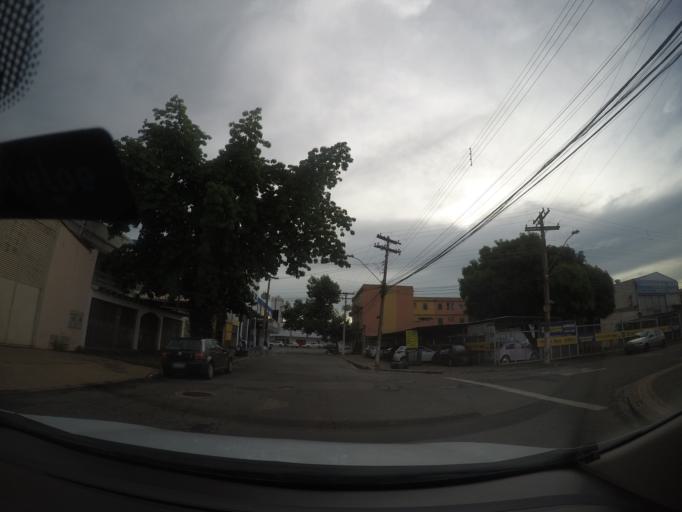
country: BR
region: Goias
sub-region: Goiania
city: Goiania
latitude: -16.6742
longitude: -49.2799
